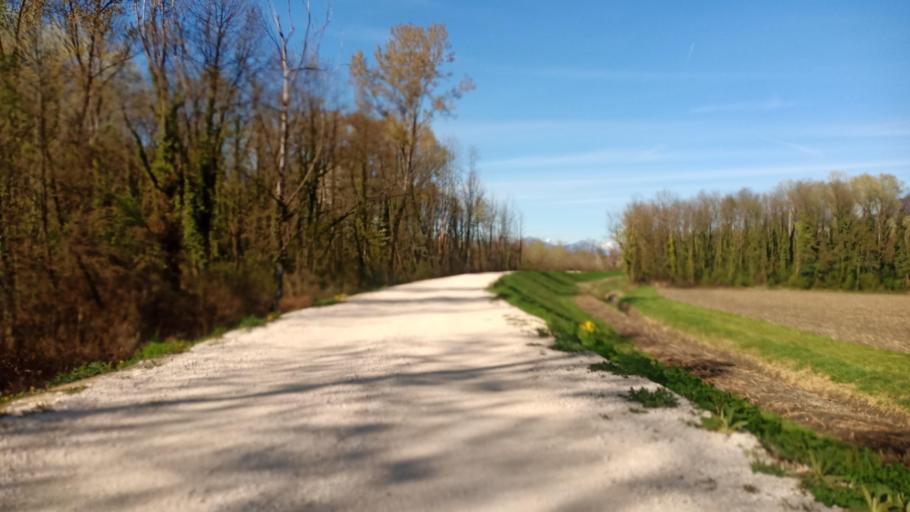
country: FR
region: Rhone-Alpes
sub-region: Departement de l'Isere
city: Tencin
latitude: 45.3114
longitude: 5.9428
